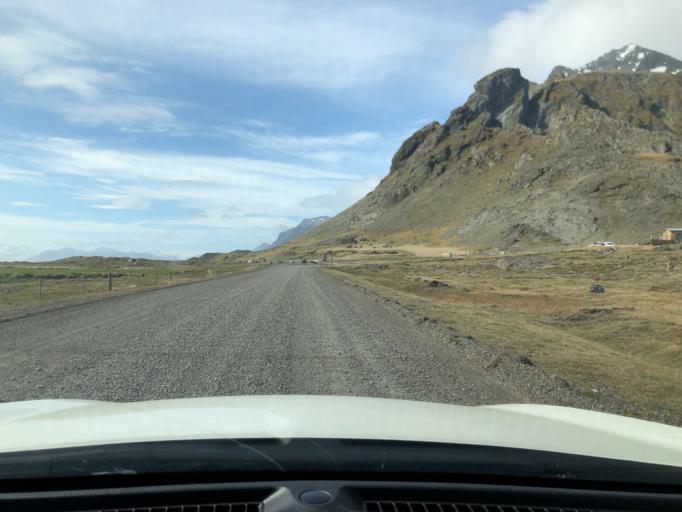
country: IS
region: East
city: Hoefn
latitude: 64.2538
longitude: -14.9930
